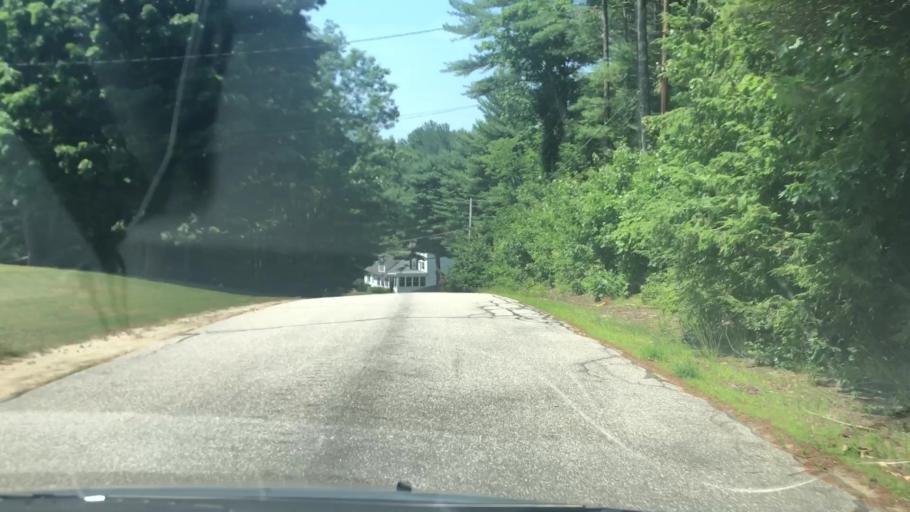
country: US
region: New Hampshire
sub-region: Hillsborough County
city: Milford
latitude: 42.8718
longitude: -71.6221
